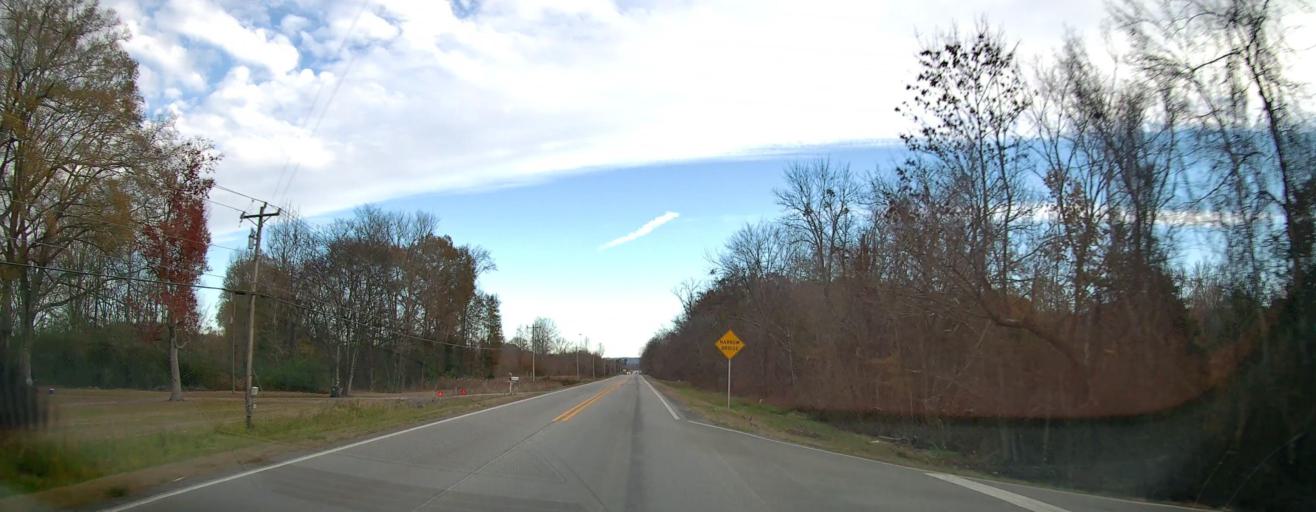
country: US
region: Alabama
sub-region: Morgan County
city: Falkville
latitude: 34.4237
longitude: -86.7184
